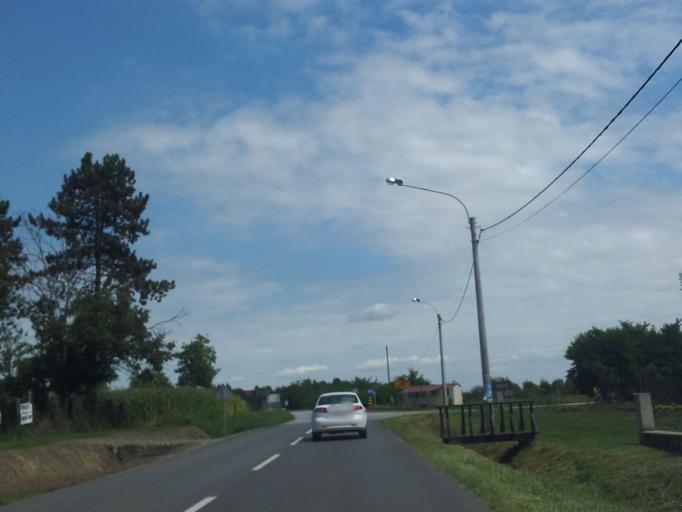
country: HR
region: Osjecko-Baranjska
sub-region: Grad Osijek
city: Bilje
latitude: 45.6080
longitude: 18.7555
